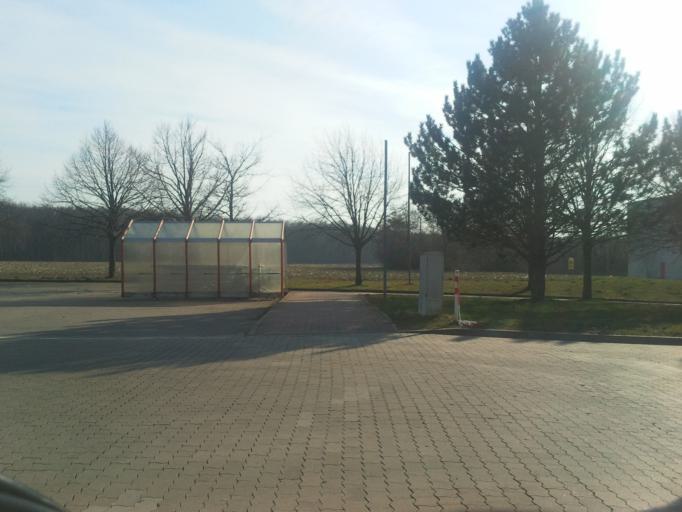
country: DE
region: Mecklenburg-Vorpommern
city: Lambrechtshagen
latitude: 54.1059
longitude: 12.0378
